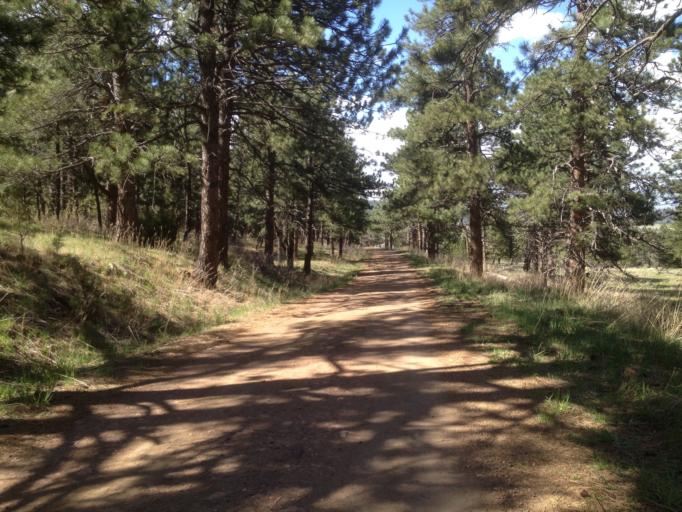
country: US
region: Colorado
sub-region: Boulder County
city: Boulder
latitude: 39.9210
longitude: -105.2711
